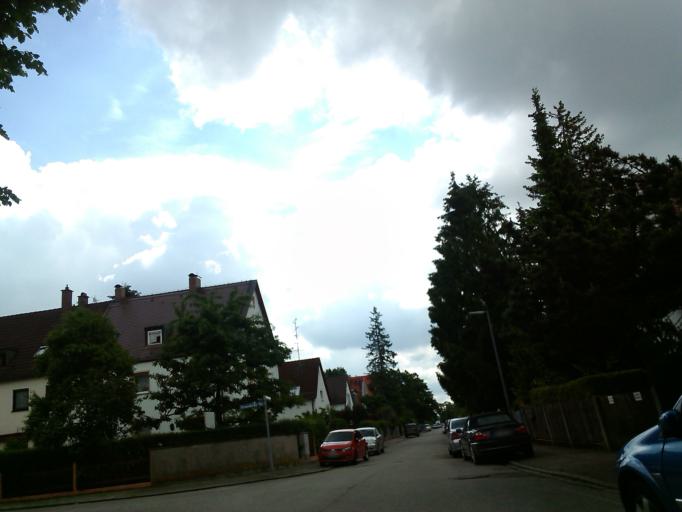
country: DE
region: Bavaria
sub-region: Upper Bavaria
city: Bogenhausen
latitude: 48.1239
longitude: 11.6439
